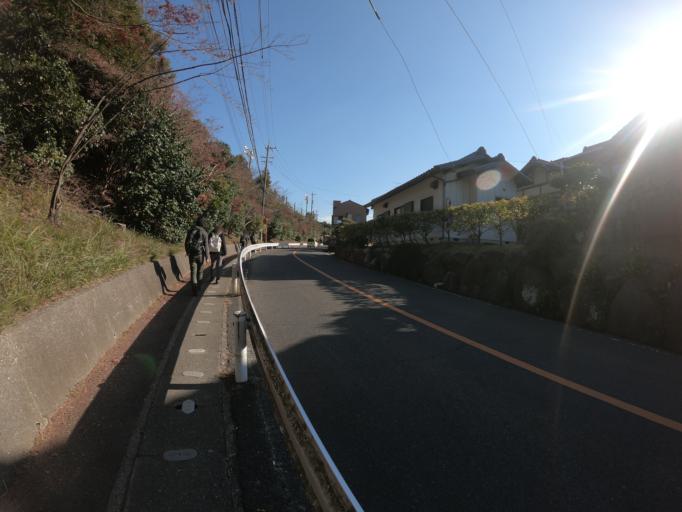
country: JP
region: Aichi
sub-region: Toyota-shi
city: Toyota
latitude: 35.1247
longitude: 137.0426
